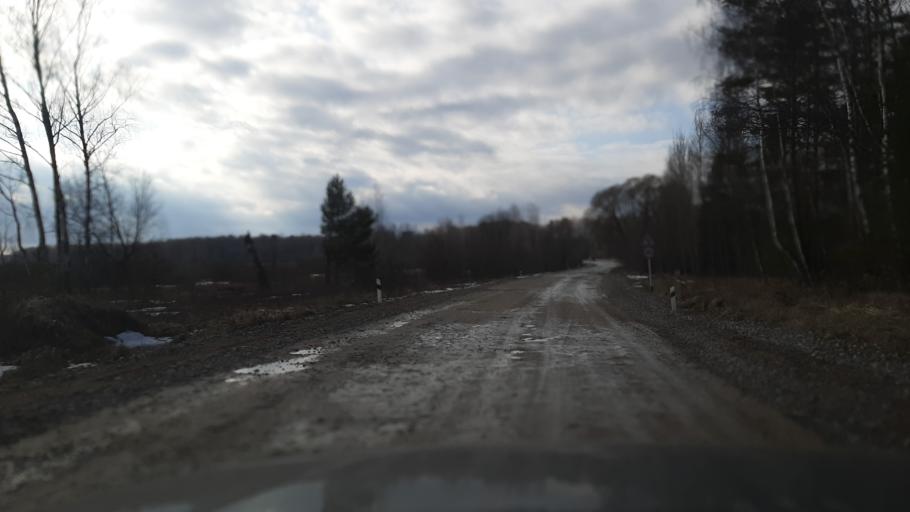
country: RU
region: Ivanovo
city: Teykovo
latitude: 56.8834
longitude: 40.6293
